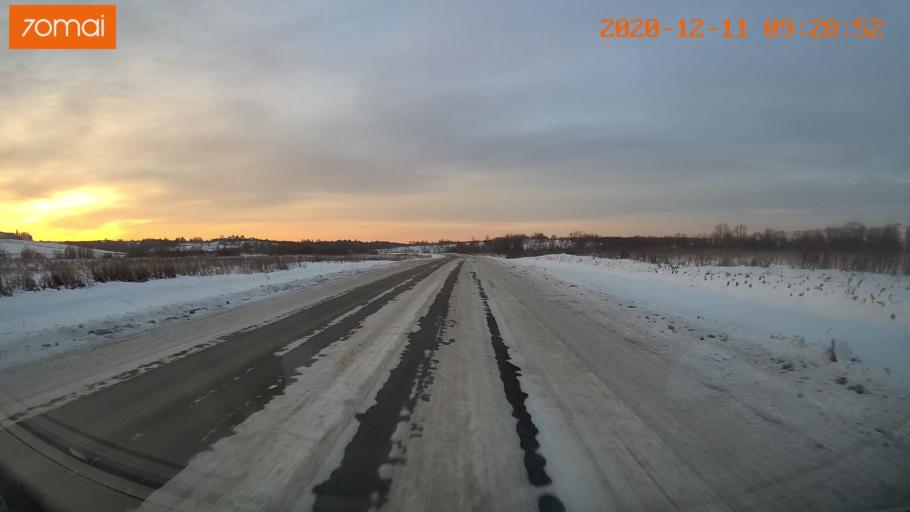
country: RU
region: Vologda
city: Vologda
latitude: 59.1486
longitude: 40.0053
